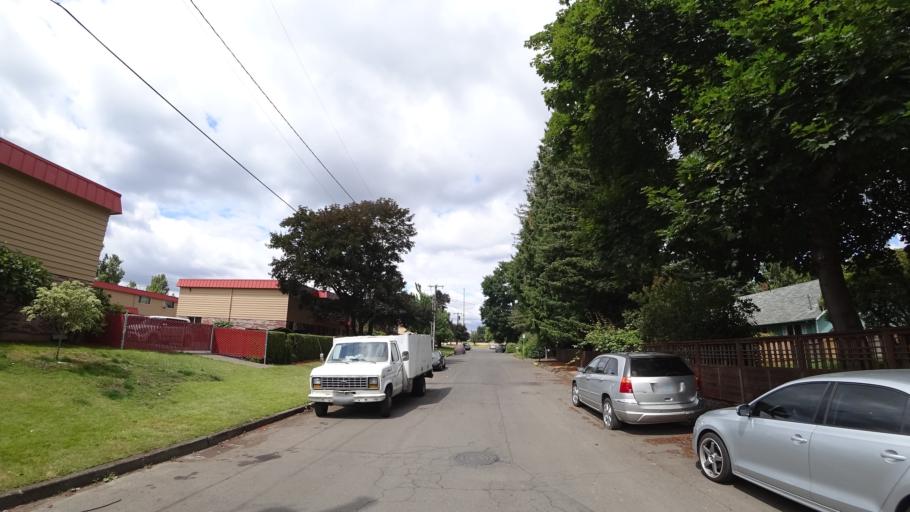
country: US
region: Oregon
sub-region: Multnomah County
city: Portland
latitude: 45.5643
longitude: -122.6185
